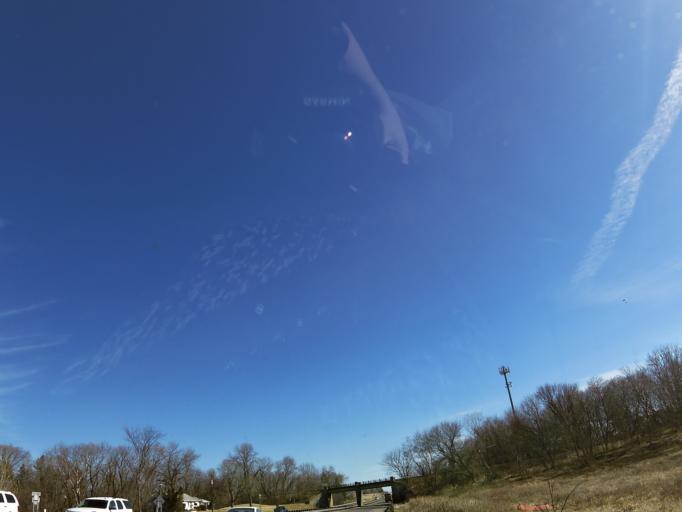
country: US
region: Minnesota
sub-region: Hennepin County
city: Corcoran
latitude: 45.0431
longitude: -93.5246
